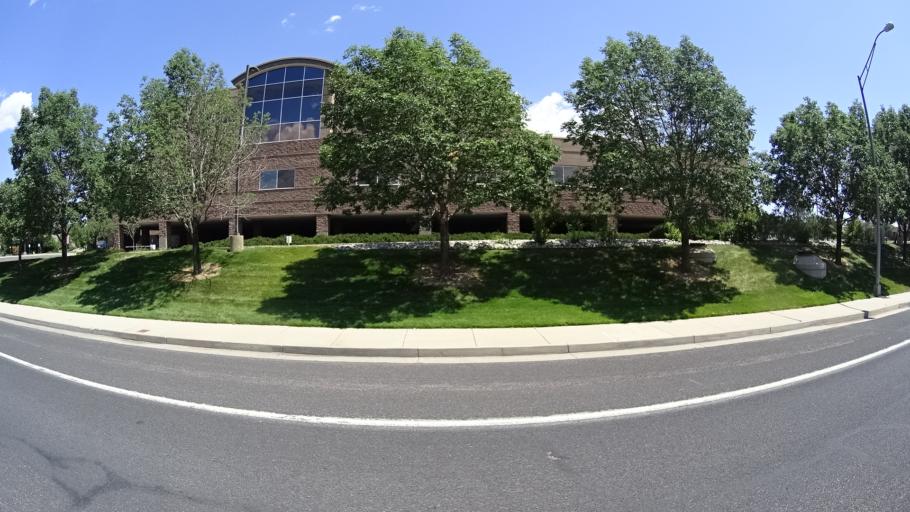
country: US
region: Colorado
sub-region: El Paso County
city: Colorado Springs
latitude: 38.8728
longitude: -104.7948
